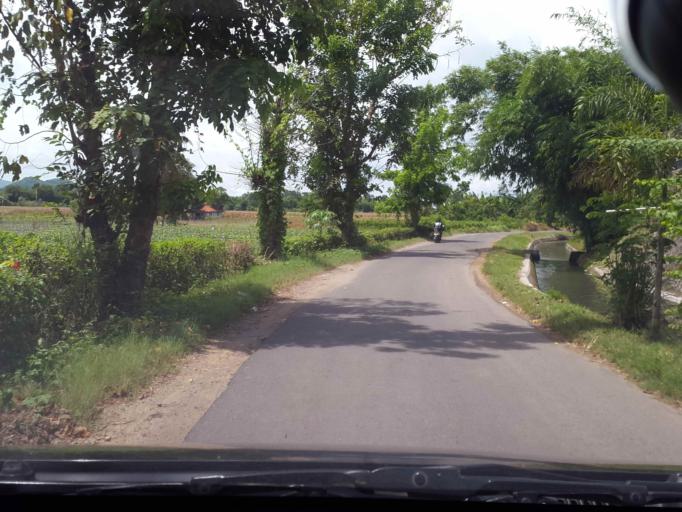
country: ID
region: West Nusa Tenggara
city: Jelateng Timur
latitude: -8.6928
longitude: 116.1082
